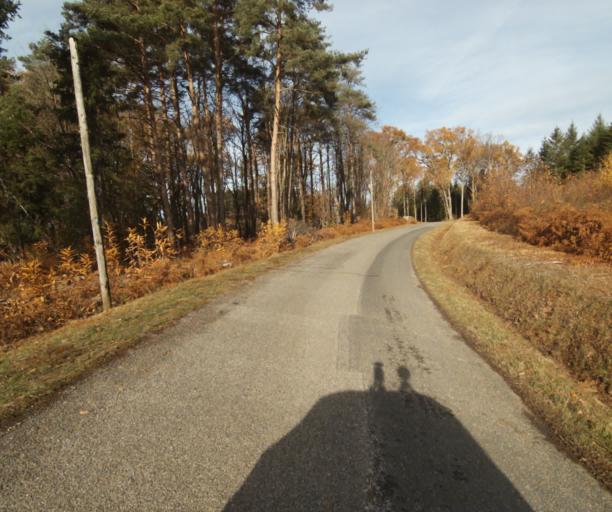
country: FR
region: Limousin
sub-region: Departement de la Correze
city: Sainte-Fortunade
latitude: 45.1873
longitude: 1.7388
